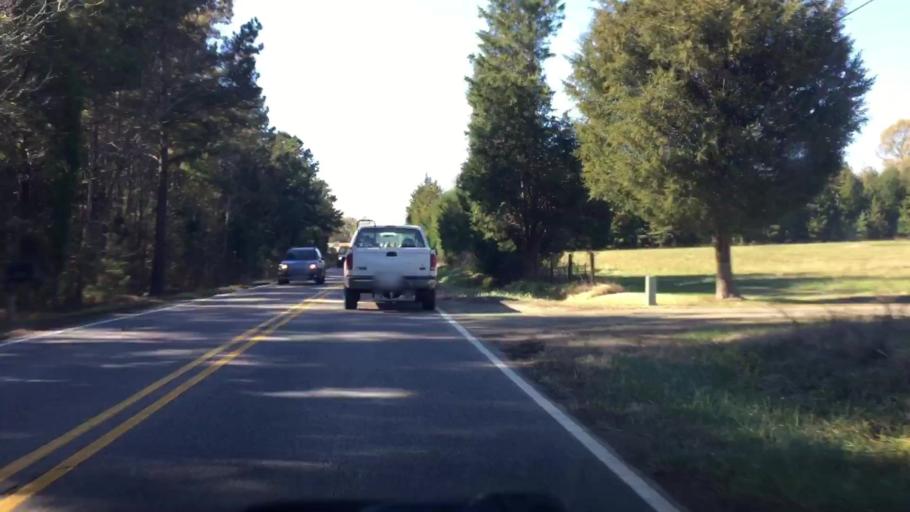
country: US
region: North Carolina
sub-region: Iredell County
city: Mooresville
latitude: 35.6195
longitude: -80.7274
